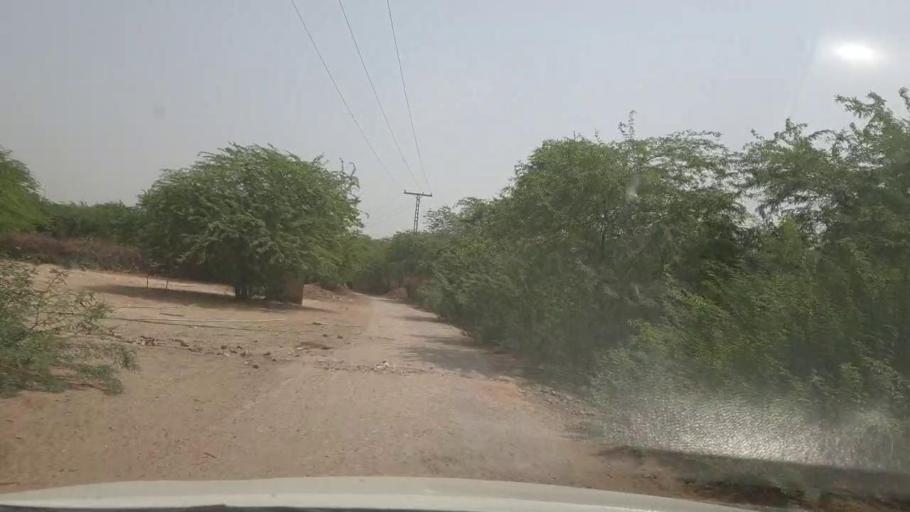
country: PK
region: Sindh
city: Kot Diji
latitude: 27.3465
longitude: 68.7174
